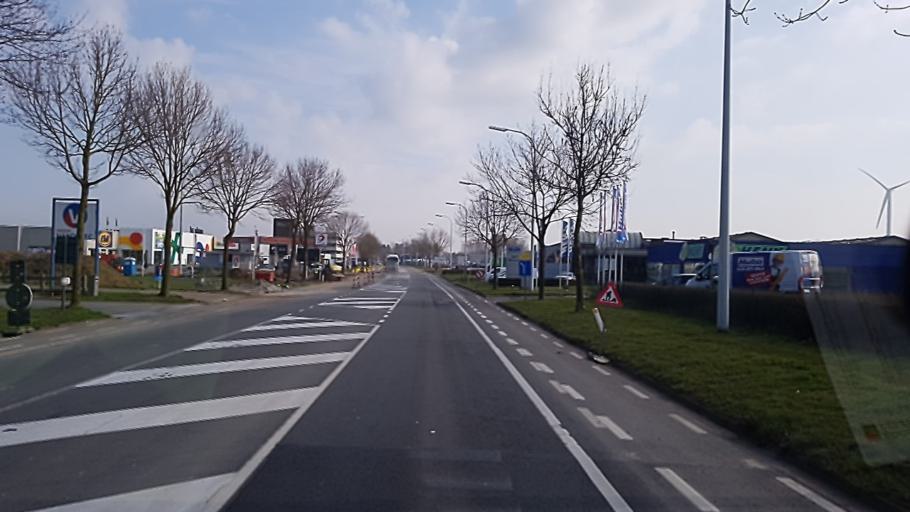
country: BE
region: Flanders
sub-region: Provincie West-Vlaanderen
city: Poperinge
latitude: 50.8500
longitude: 2.7415
